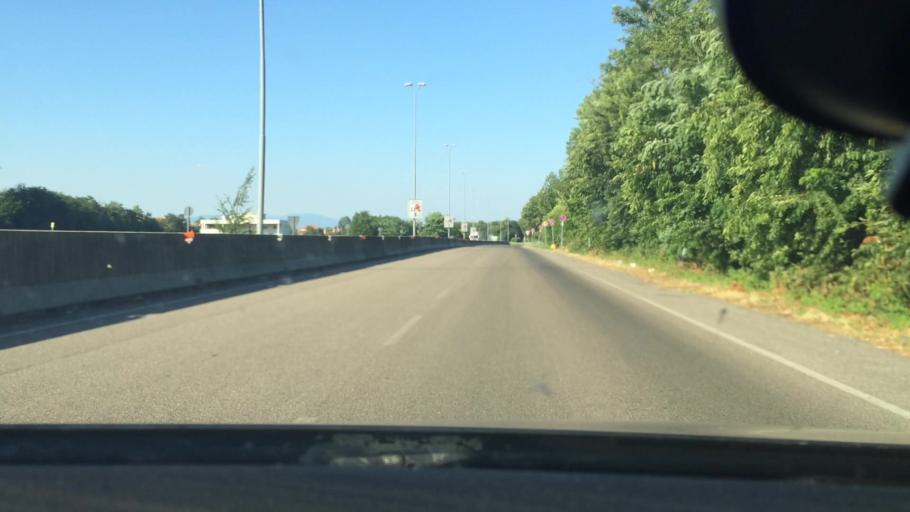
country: IT
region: Lombardy
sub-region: Citta metropolitana di Milano
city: Cerro Maggiore
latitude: 45.6056
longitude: 8.9495
